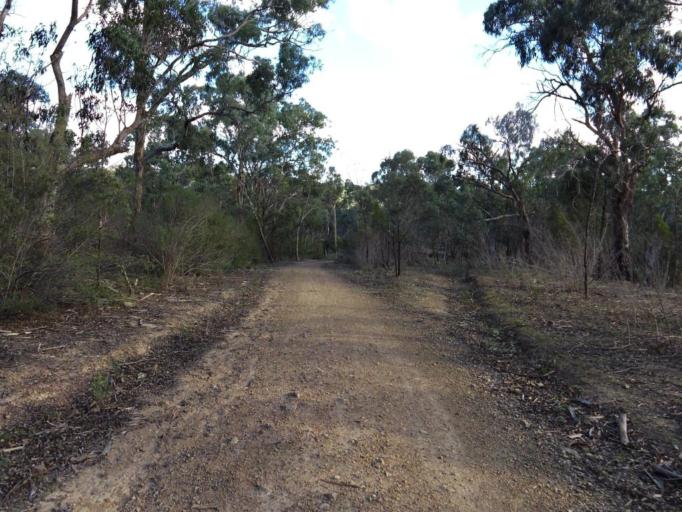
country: AU
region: Victoria
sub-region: Nillumbik
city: North Warrandyte
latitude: -37.7381
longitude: 145.2008
